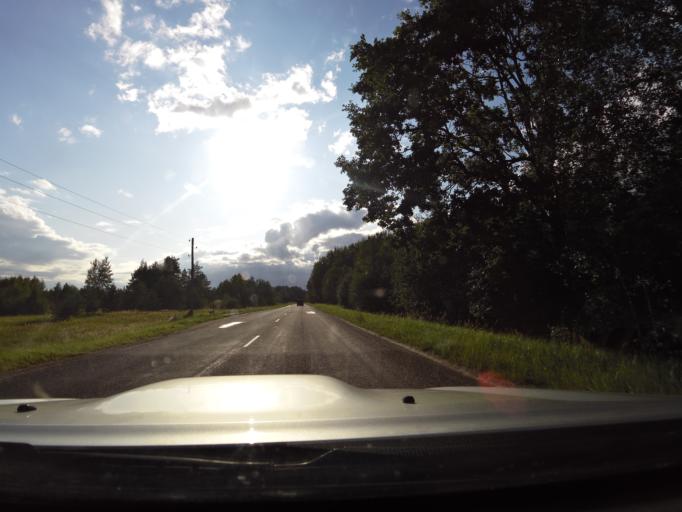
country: LV
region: Nereta
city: Nereta
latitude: 56.1837
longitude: 25.3790
